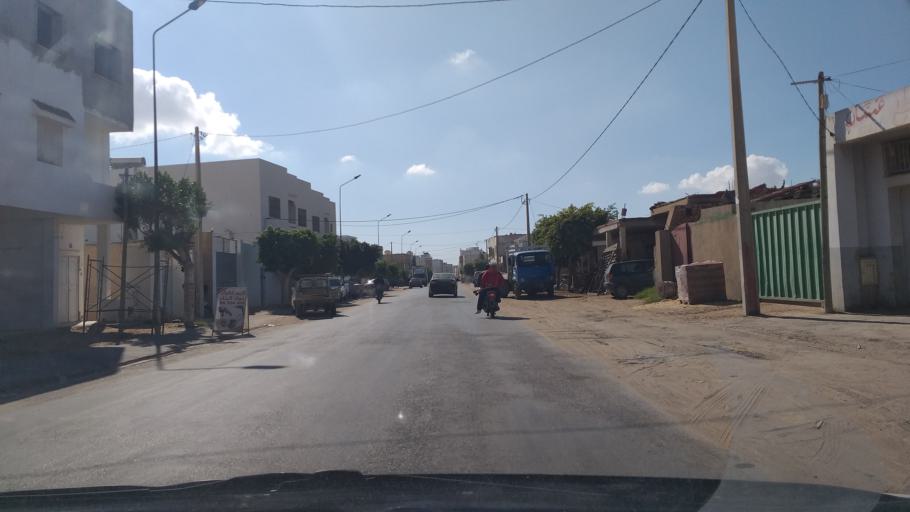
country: TN
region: Safaqis
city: Al Qarmadah
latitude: 34.8030
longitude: 10.7811
